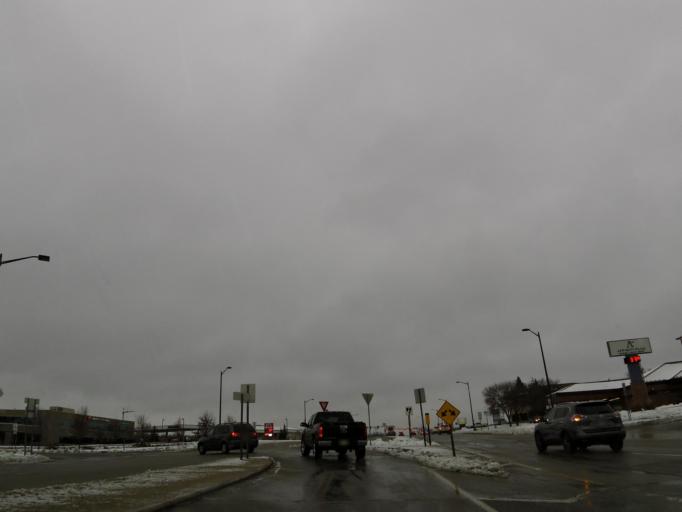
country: US
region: Minnesota
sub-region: Dakota County
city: Lakeville
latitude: 44.6960
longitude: -93.2863
